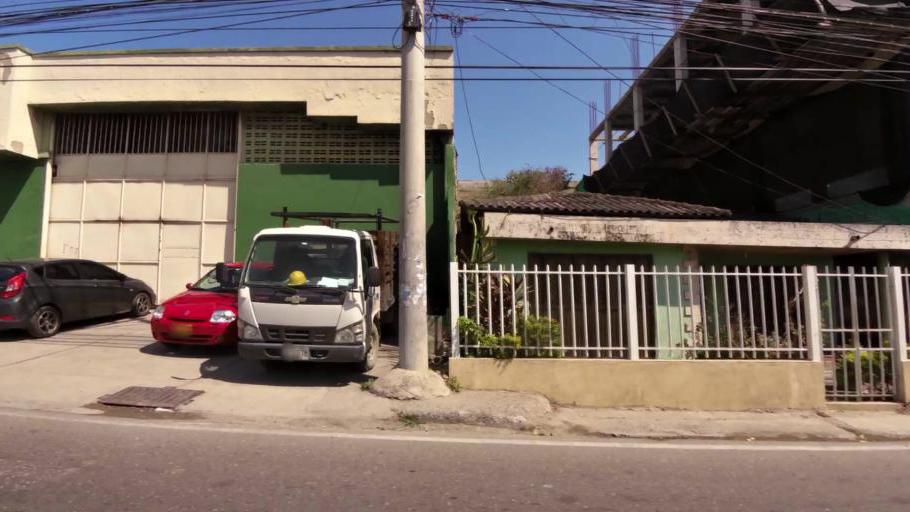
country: CO
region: Bolivar
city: Cartagena
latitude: 10.3876
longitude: -75.5112
